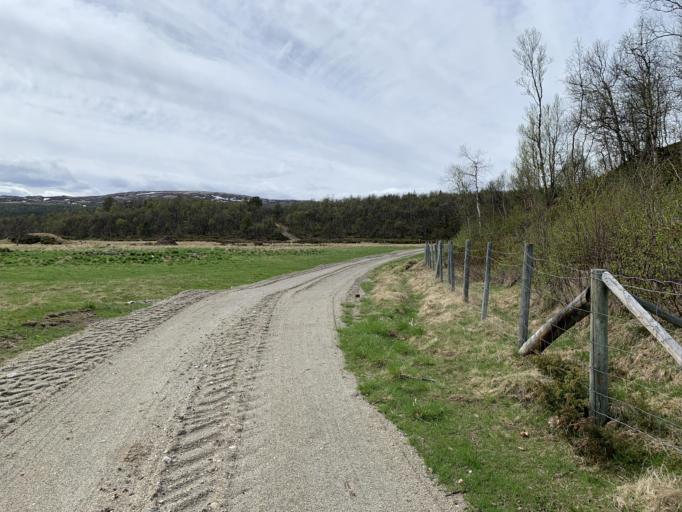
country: NO
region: Hedmark
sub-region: Alvdal
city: Alvdal
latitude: 62.4122
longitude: 10.4021
